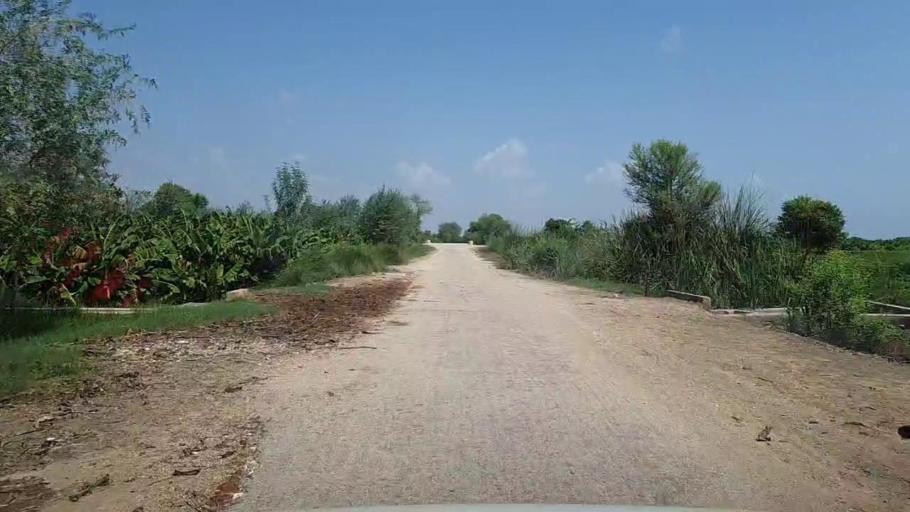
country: PK
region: Sindh
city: Bhiria
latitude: 26.8694
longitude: 68.2570
